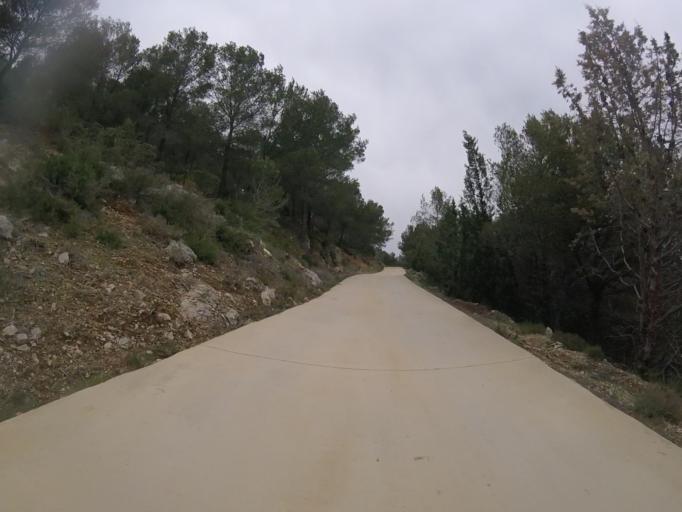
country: ES
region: Valencia
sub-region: Provincia de Castello
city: Alcala de Xivert
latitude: 40.3021
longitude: 0.2572
